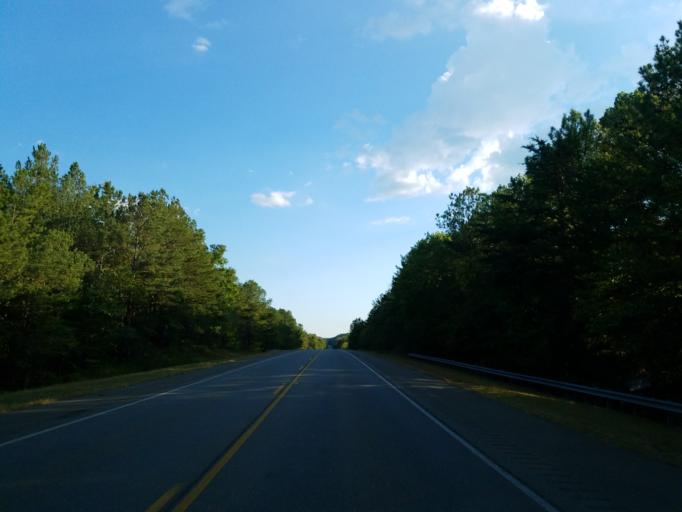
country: US
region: Georgia
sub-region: Murray County
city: Chatsworth
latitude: 34.6307
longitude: -84.7139
